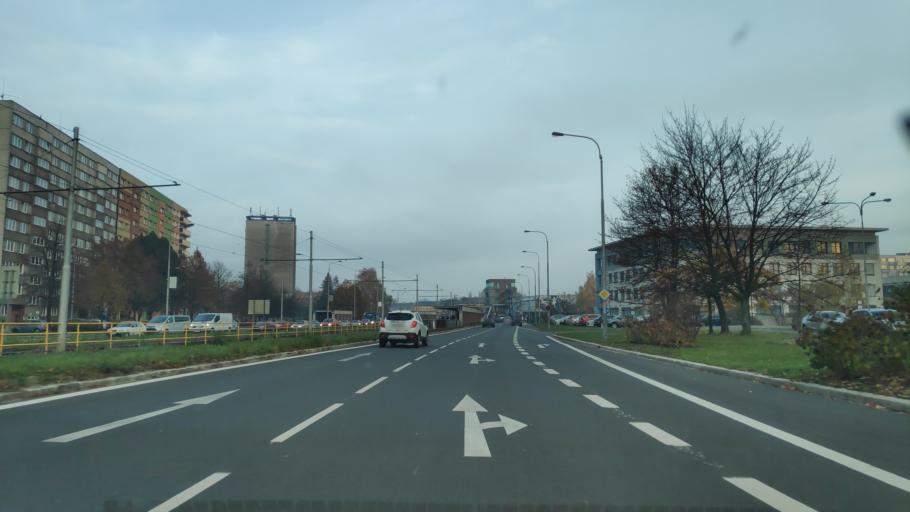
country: CZ
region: Moravskoslezsky
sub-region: Okres Ostrava-Mesto
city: Ostrava
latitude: 49.7855
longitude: 18.2565
